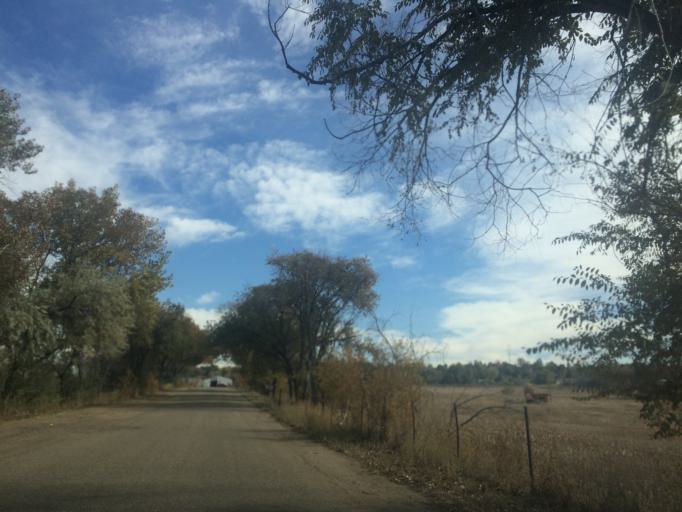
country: US
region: Colorado
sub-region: Boulder County
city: Gunbarrel
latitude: 40.0125
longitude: -105.2054
